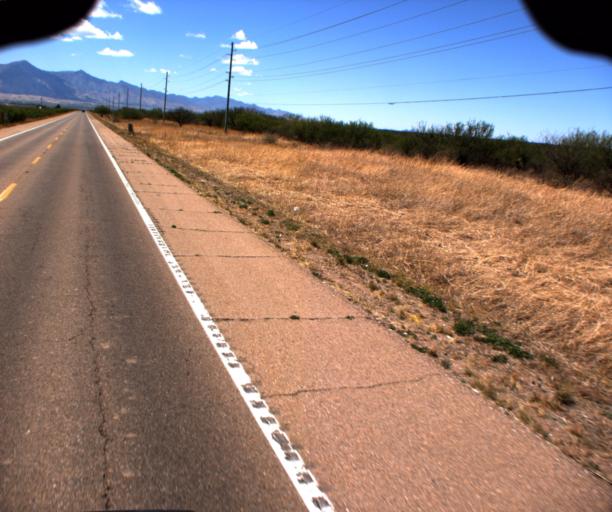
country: US
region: Arizona
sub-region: Cochise County
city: Naco
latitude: 31.3779
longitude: -110.0226
